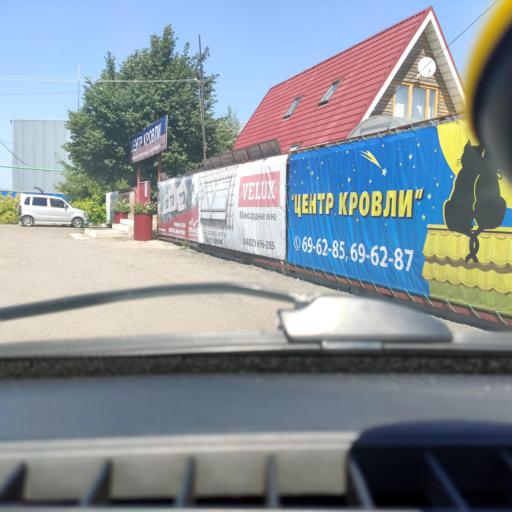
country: RU
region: Samara
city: Tol'yatti
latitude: 53.5713
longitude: 49.3613
